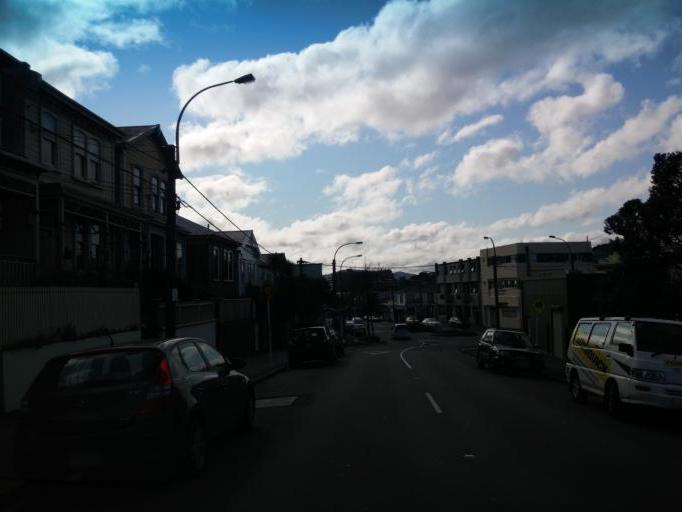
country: NZ
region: Wellington
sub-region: Wellington City
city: Brooklyn
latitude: -41.3174
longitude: 174.7805
